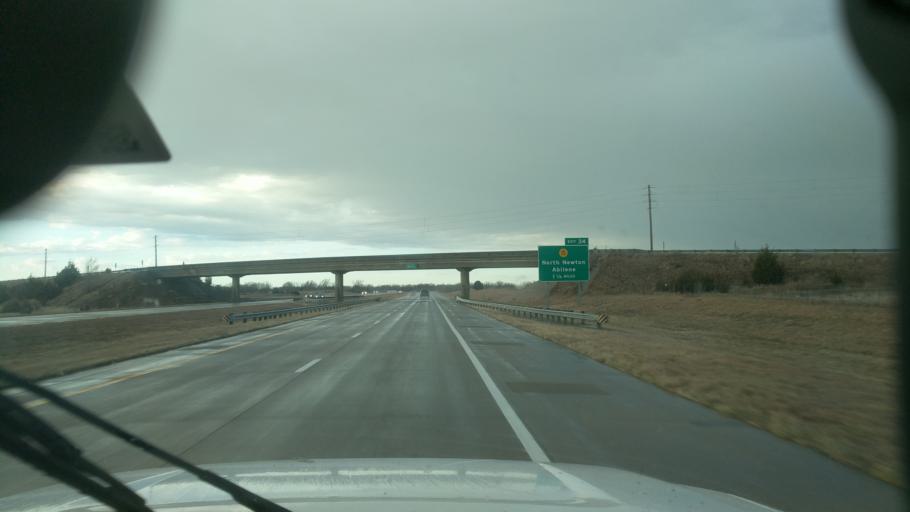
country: US
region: Kansas
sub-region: Harvey County
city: North Newton
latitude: 38.0709
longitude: -97.3262
